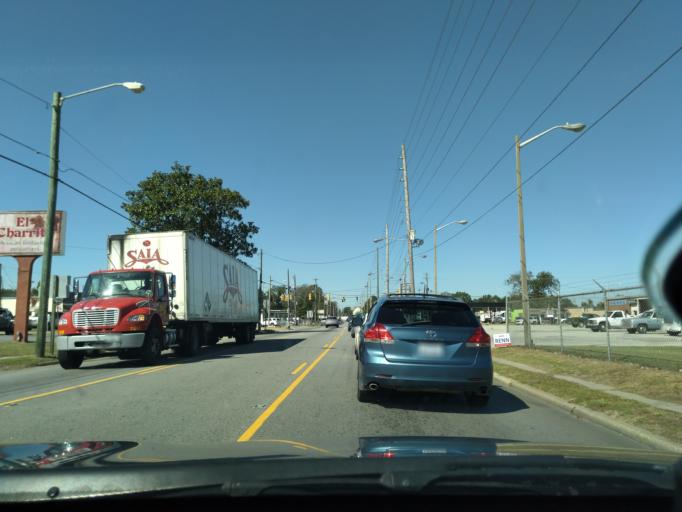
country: US
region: North Carolina
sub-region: Beaufort County
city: Washington
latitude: 35.5490
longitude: -77.0568
